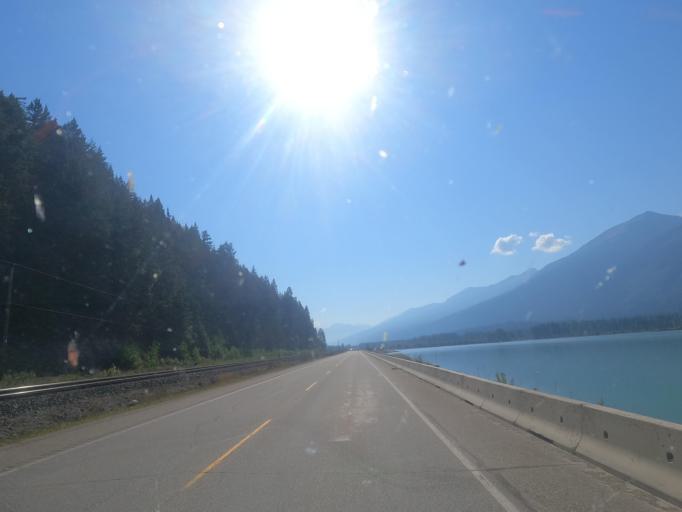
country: CA
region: Alberta
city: Jasper Park Lodge
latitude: 52.9405
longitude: -118.8500
